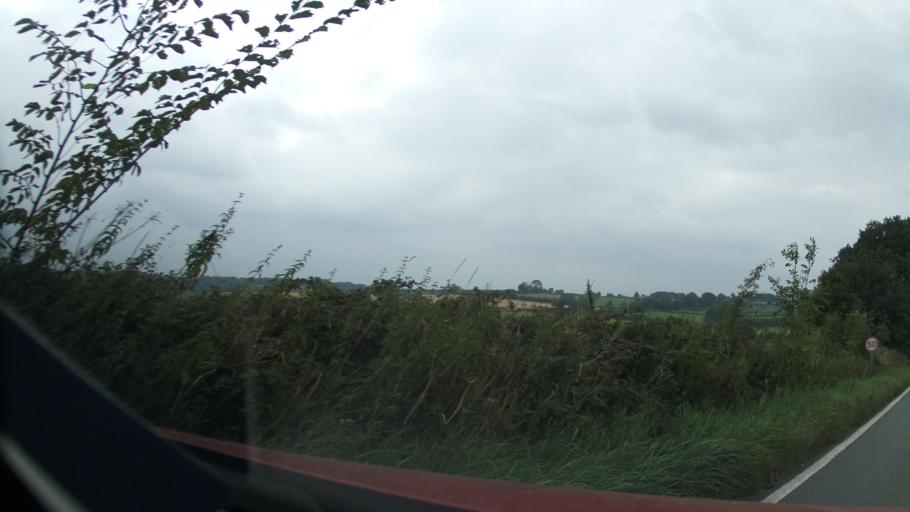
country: GB
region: England
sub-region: Derbyshire
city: Wirksworth
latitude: 53.0165
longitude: -1.5869
